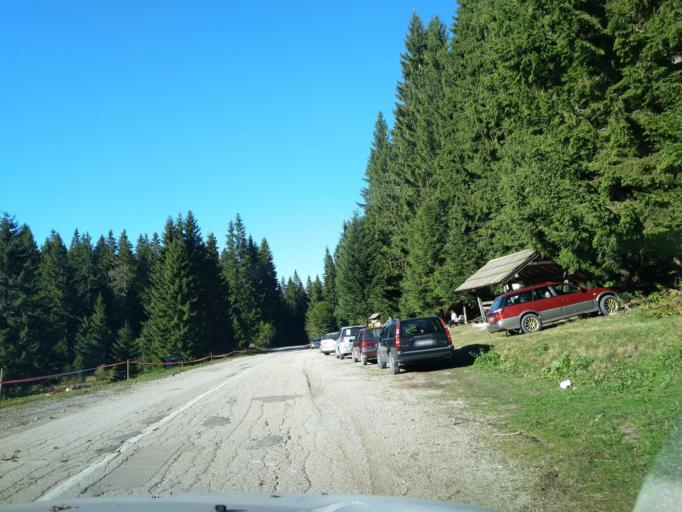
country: RS
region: Central Serbia
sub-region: Moravicki Okrug
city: Ivanjica
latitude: 43.4233
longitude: 20.2637
